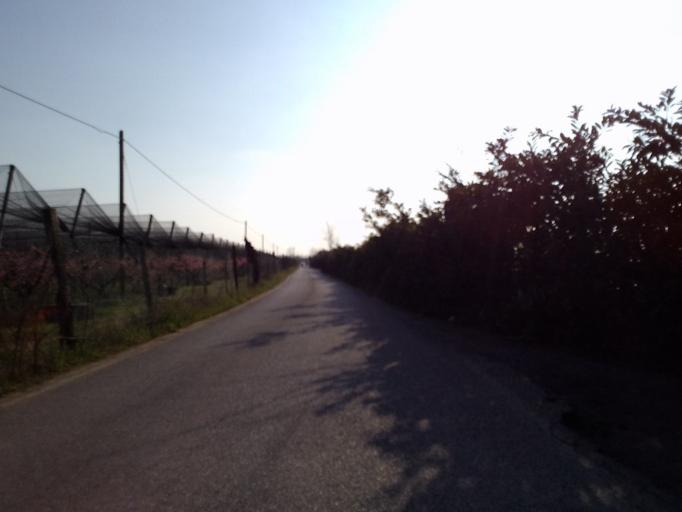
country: IT
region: Veneto
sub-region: Provincia di Verona
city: Dossobuono
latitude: 45.3861
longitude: 10.9157
